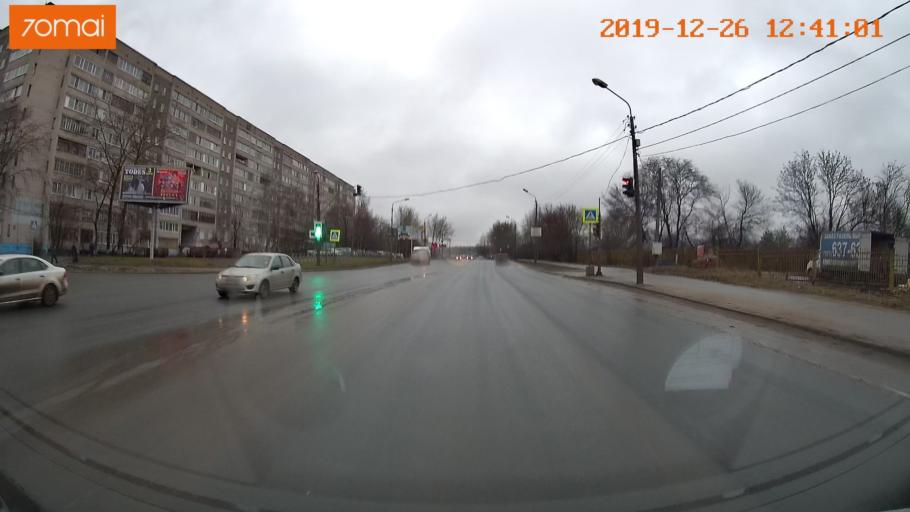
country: RU
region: Vologda
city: Tonshalovo
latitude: 59.1460
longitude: 37.9664
